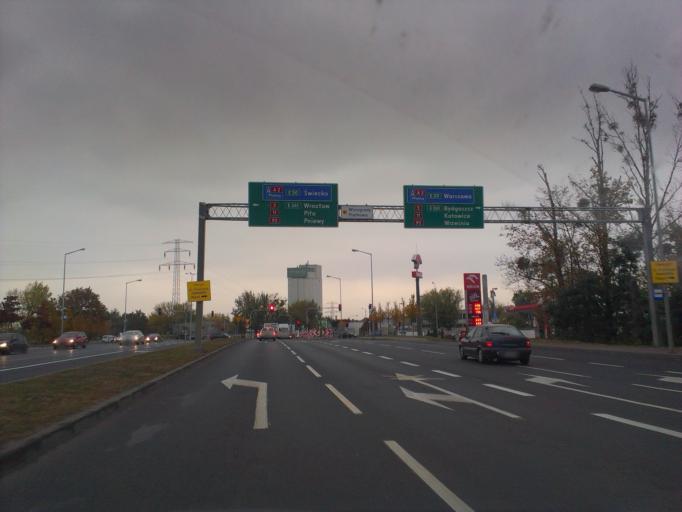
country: PL
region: Greater Poland Voivodeship
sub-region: Poznan
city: Poznan
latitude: 52.4263
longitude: 16.9660
